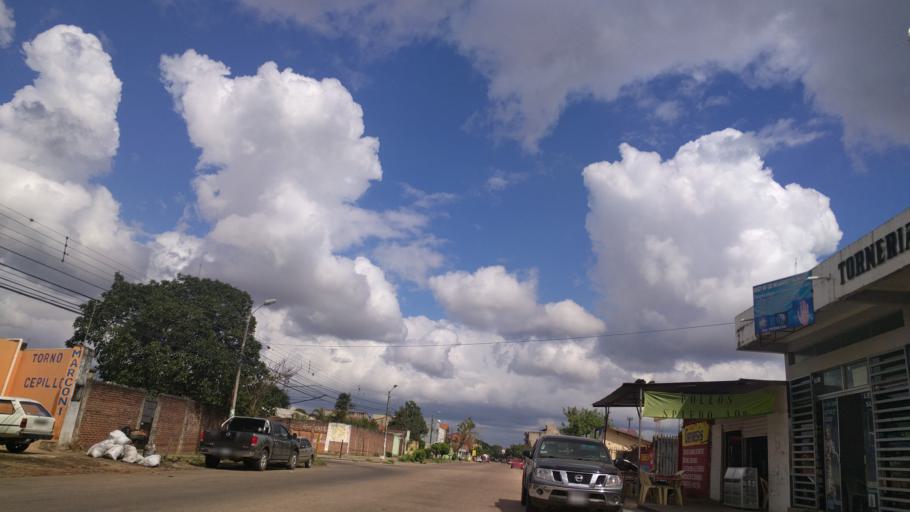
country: BO
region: Santa Cruz
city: Santa Cruz de la Sierra
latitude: -17.8089
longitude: -63.2009
